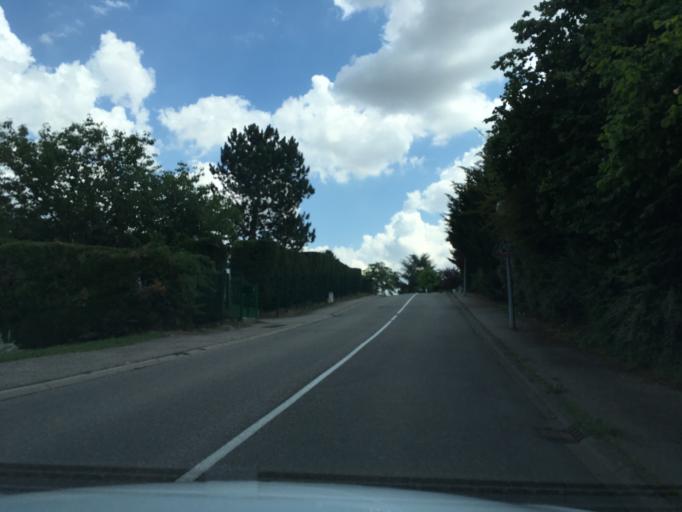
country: FR
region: Lorraine
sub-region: Departement de la Moselle
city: Saint-Julien-les-Metz
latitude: 49.1292
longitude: 6.2022
